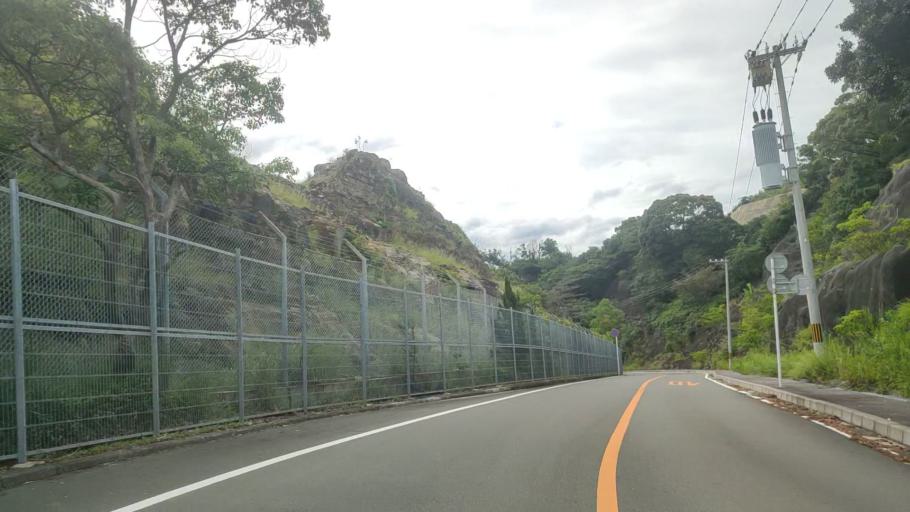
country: JP
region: Wakayama
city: Tanabe
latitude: 33.6648
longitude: 135.3680
